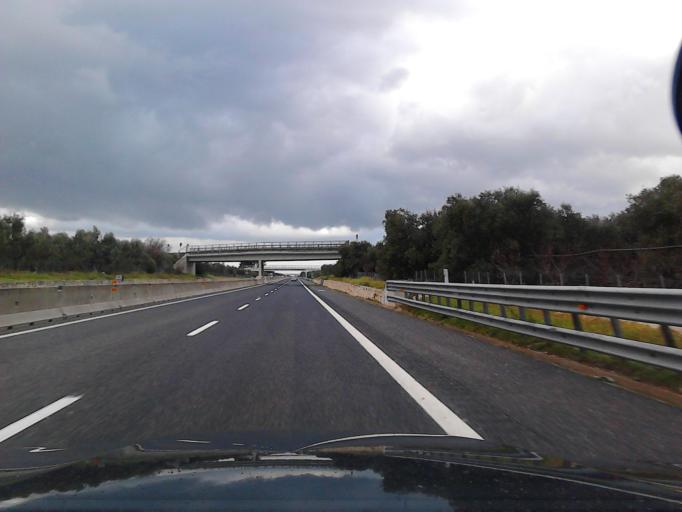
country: IT
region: Apulia
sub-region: Provincia di Bari
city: Molfetta
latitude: 41.1797
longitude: 16.5548
